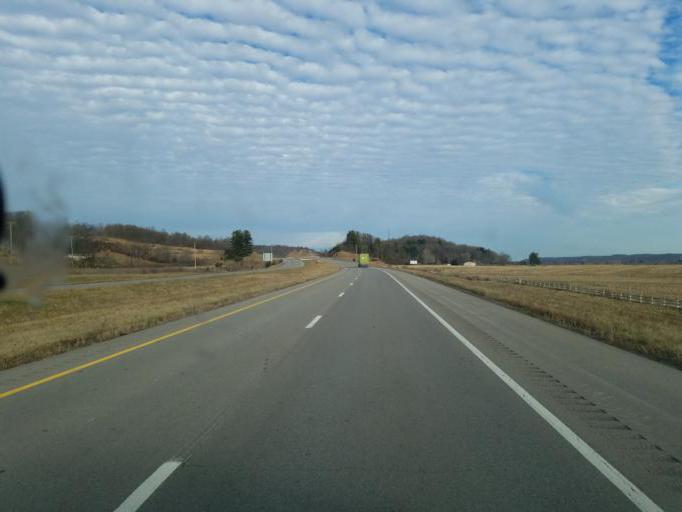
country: US
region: Ohio
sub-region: Muskingum County
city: Frazeysburg
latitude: 40.1136
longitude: -82.1596
